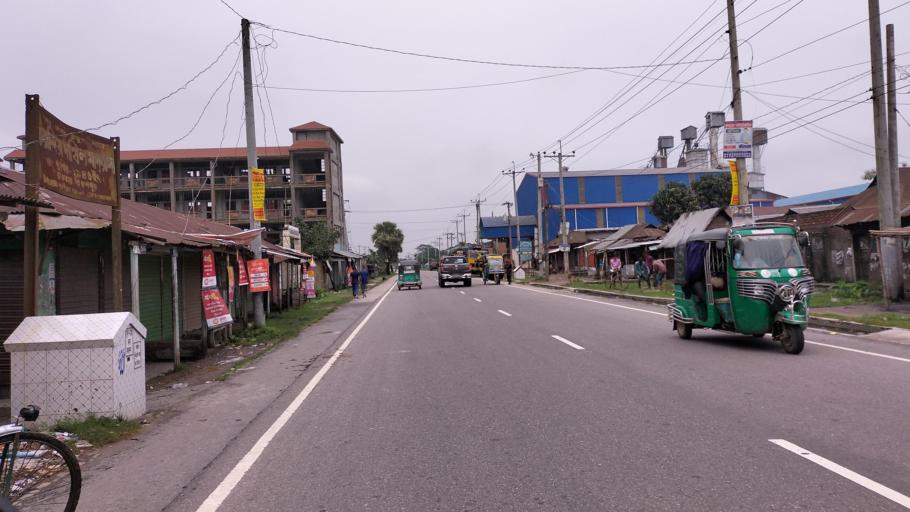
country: BD
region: Dhaka
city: Netrakona
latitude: 24.8510
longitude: 90.6273
